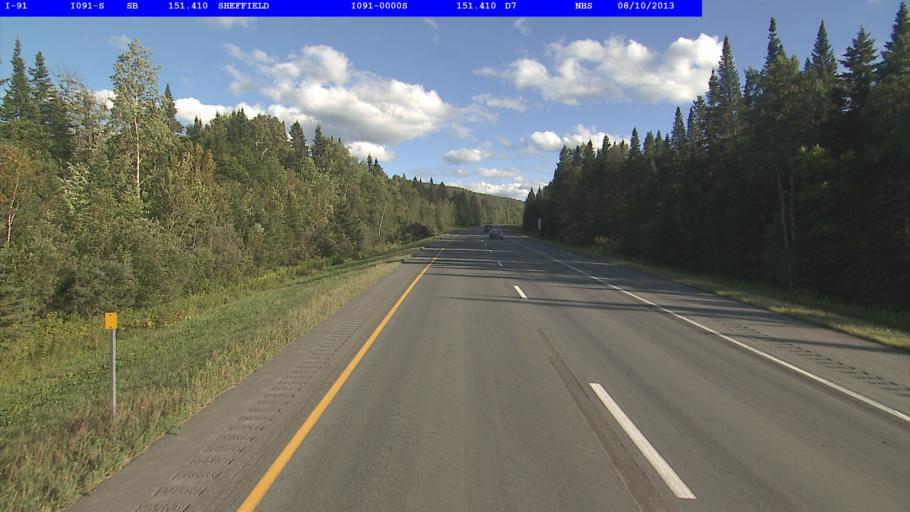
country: US
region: Vermont
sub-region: Caledonia County
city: Lyndonville
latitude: 44.6849
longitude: -72.1350
